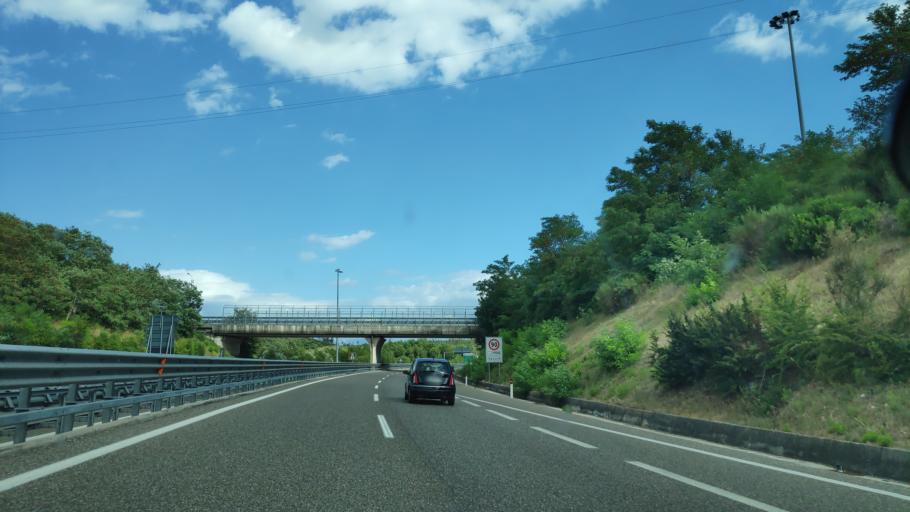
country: IT
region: Campania
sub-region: Provincia di Salerno
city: Sicignano degli Alburni
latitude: 40.6095
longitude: 15.2944
